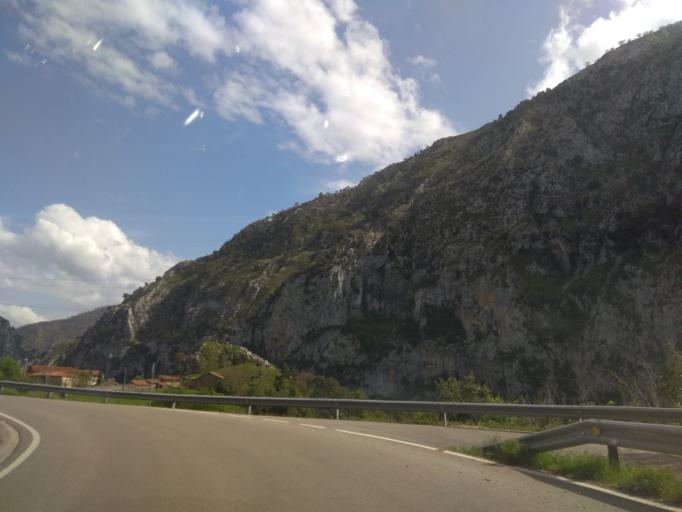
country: ES
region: Cantabria
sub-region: Provincia de Cantabria
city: Tresviso
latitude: 43.2536
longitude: -4.6022
